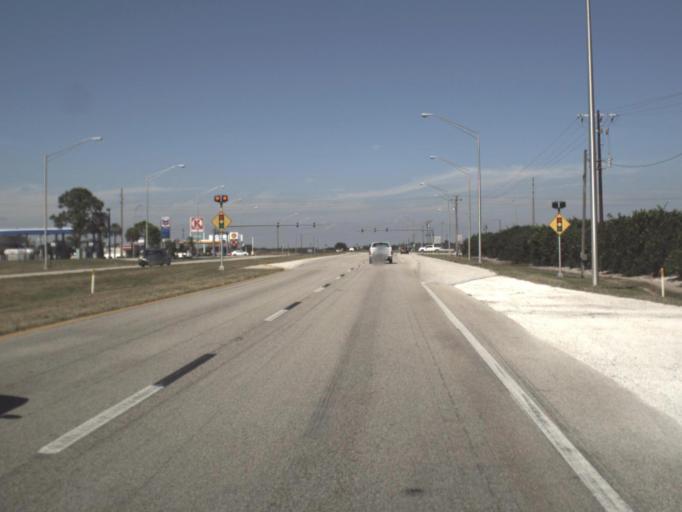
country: US
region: Florida
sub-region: Highlands County
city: Placid Lakes
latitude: 27.2061
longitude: -81.3286
